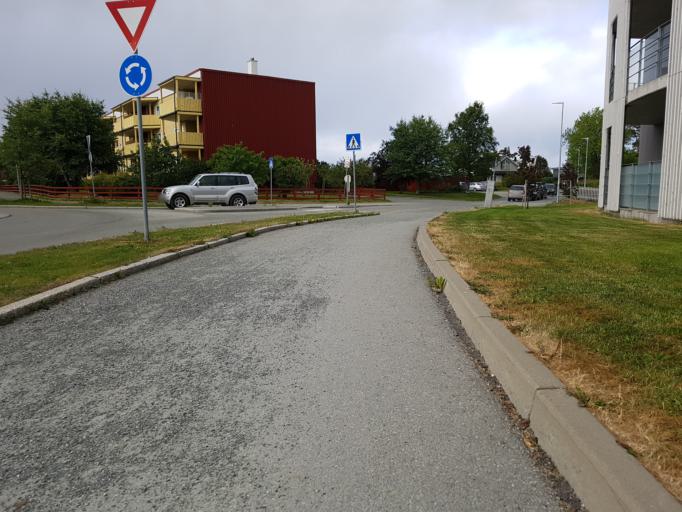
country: NO
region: Sor-Trondelag
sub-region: Trondheim
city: Trondheim
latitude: 63.4316
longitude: 10.4494
